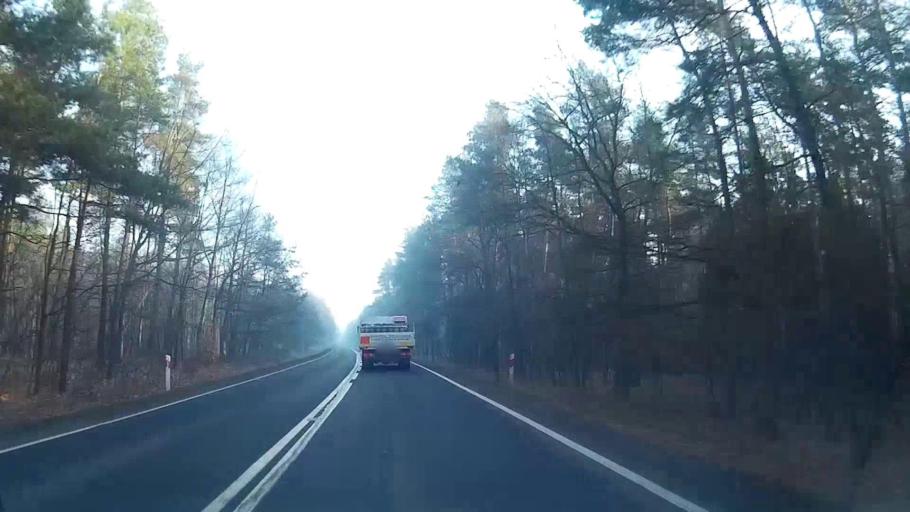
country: PL
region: Lesser Poland Voivodeship
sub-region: Powiat oswiecimski
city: Chelmek
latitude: 50.0795
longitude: 19.2758
